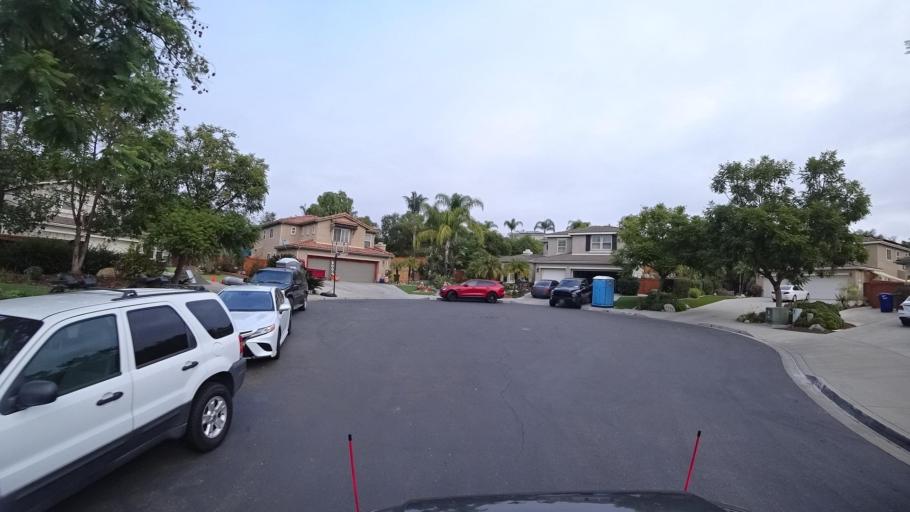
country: US
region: California
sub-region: San Diego County
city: Rancho San Diego
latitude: 32.7651
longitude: -116.9222
